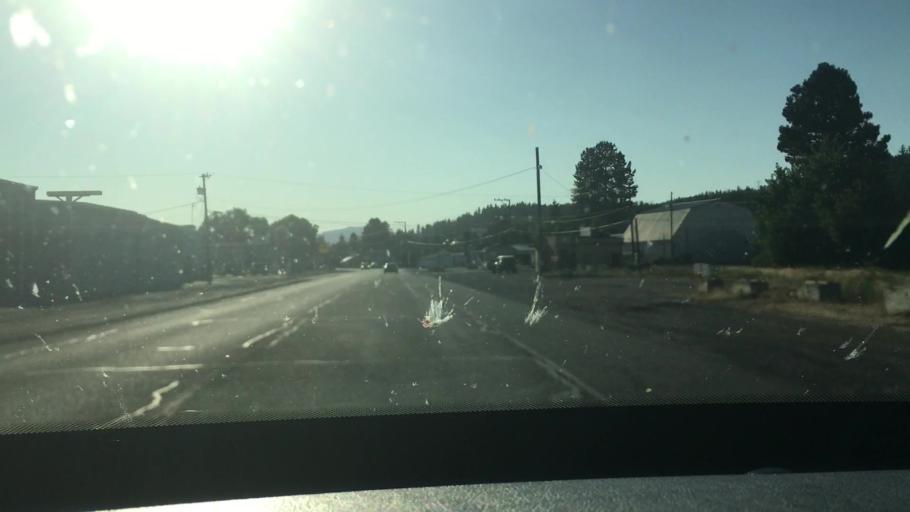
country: US
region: Washington
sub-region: Kittitas County
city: Cle Elum
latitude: 47.1915
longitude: -120.9144
